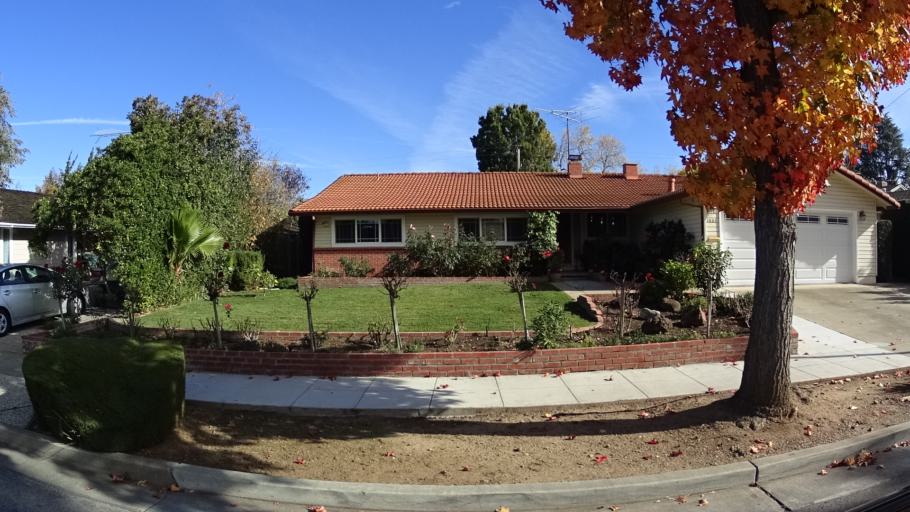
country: US
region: California
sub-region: Santa Clara County
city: Cupertino
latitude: 37.3437
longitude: -122.0480
